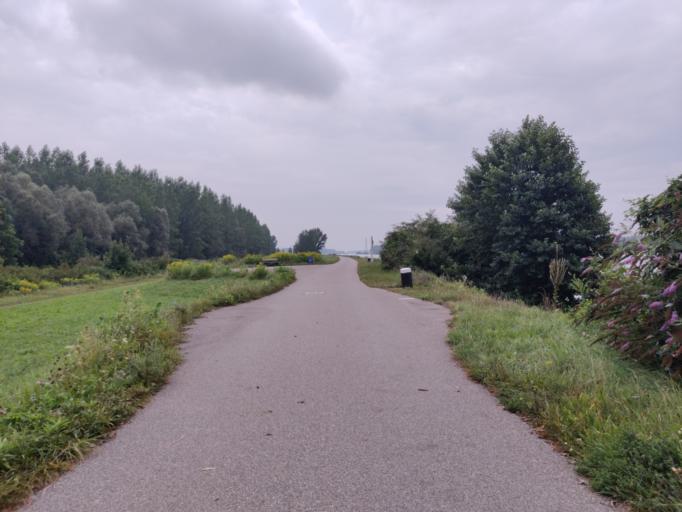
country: AT
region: Upper Austria
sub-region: Politischer Bezirk Urfahr-Umgebung
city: Steyregg
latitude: 48.2749
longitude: 14.3615
